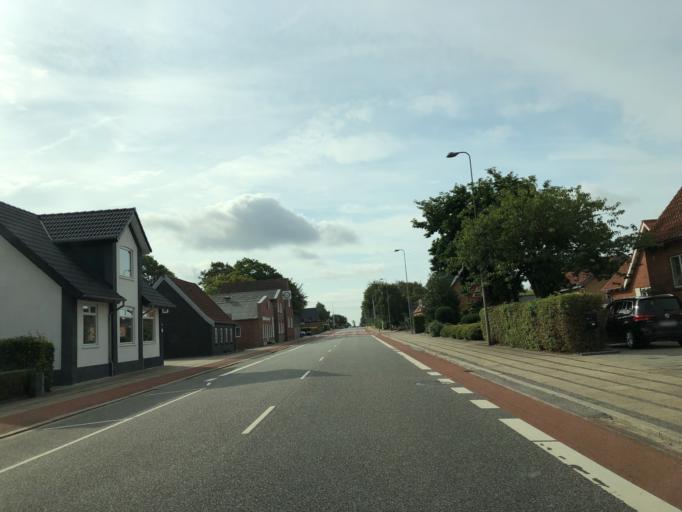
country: DK
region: Central Jutland
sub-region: Ringkobing-Skjern Kommune
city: Skjern
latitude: 55.9418
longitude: 8.4994
